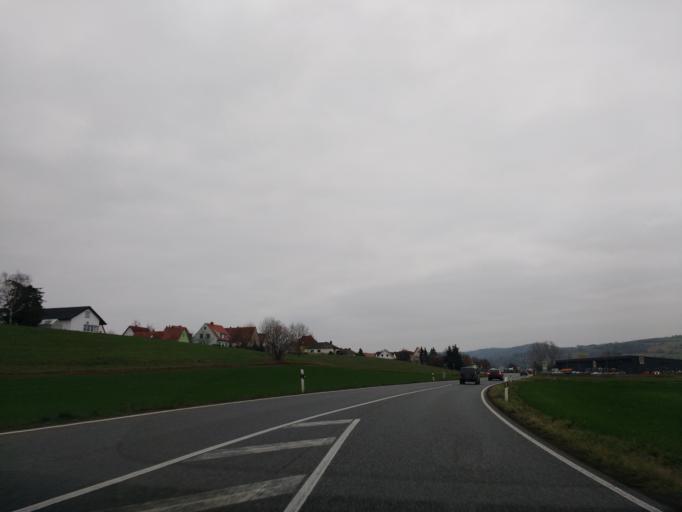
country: DE
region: Hesse
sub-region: Regierungsbezirk Kassel
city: Alheim
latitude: 51.0528
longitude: 9.6602
